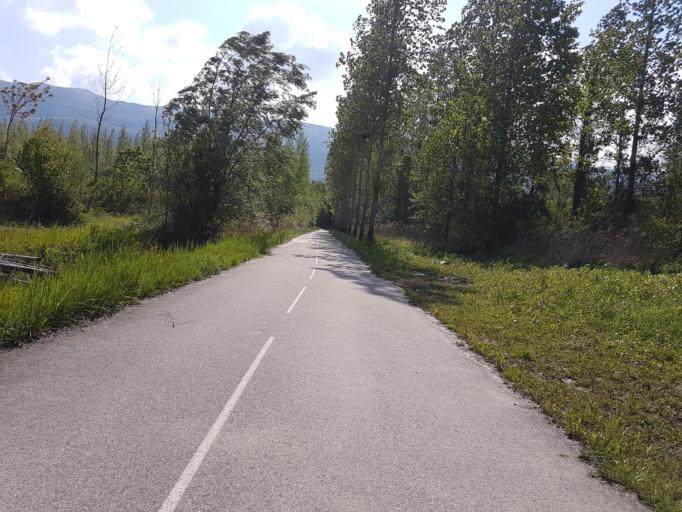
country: FR
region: Rhone-Alpes
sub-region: Departement de l'Ain
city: Culoz
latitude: 45.8647
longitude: 5.8200
